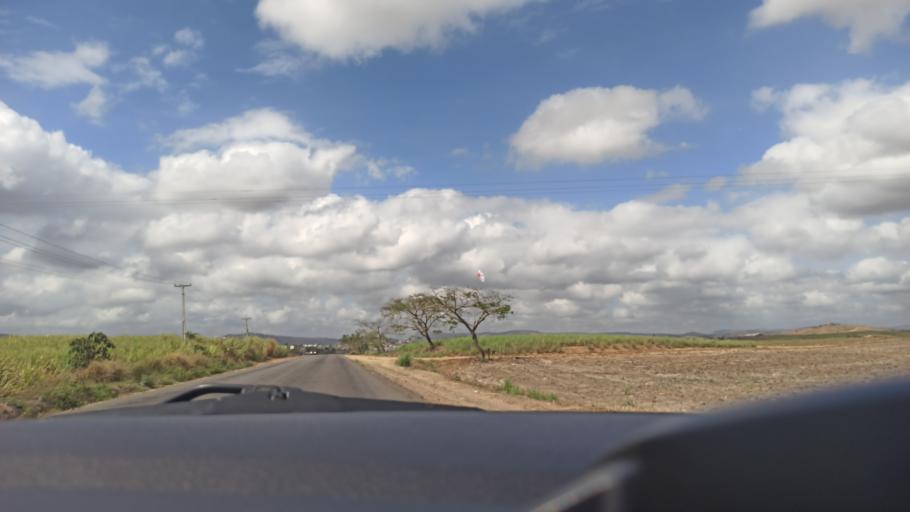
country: BR
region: Pernambuco
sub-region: Timbauba
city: Timbauba
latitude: -7.4876
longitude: -35.2940
